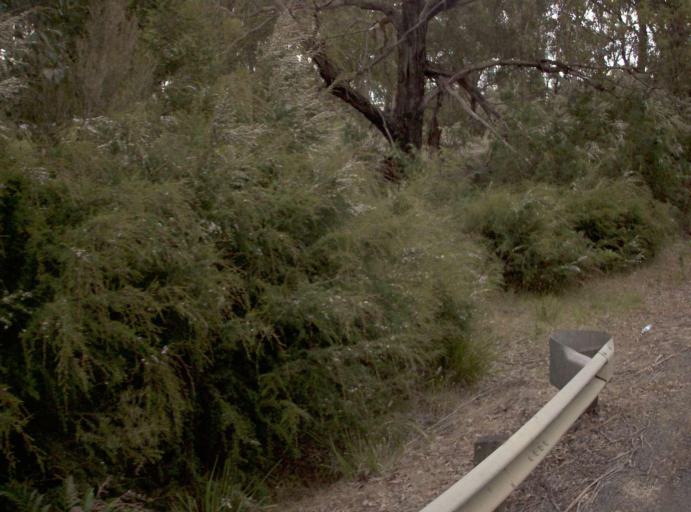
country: AU
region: Victoria
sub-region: Wellington
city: Sale
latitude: -38.3279
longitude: 147.0181
